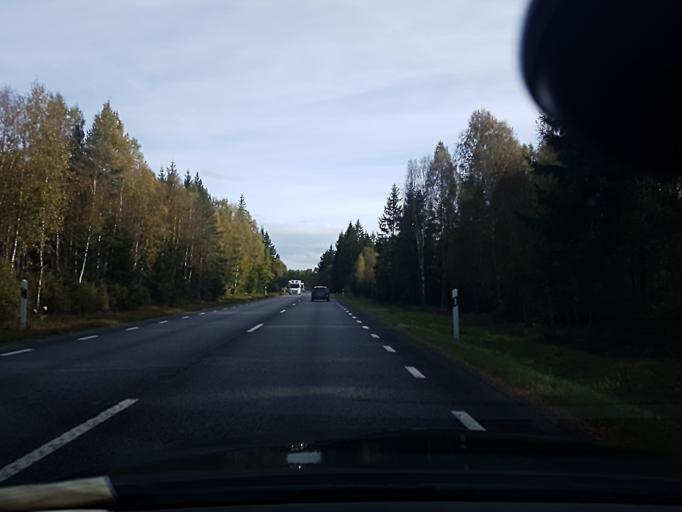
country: SE
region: Joenkoeping
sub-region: Varnamo Kommun
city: Varnamo
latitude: 57.1472
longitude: 14.0958
